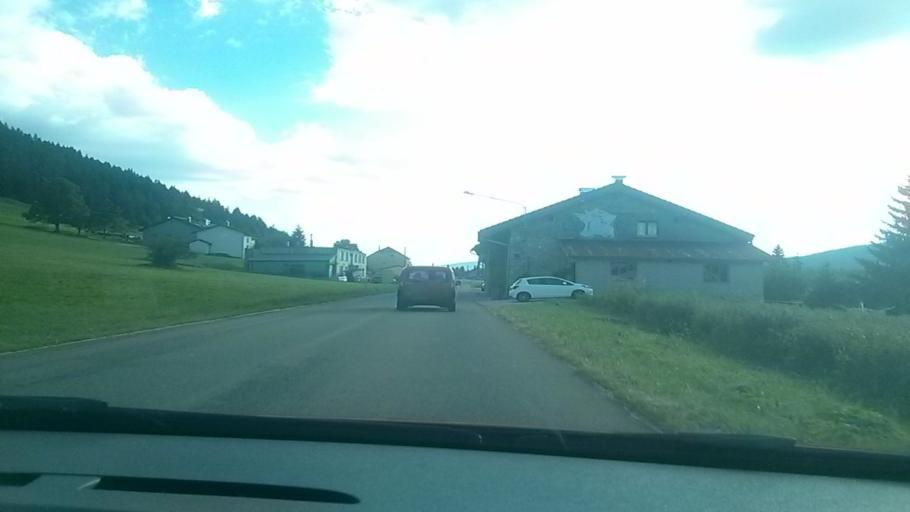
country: FR
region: Franche-Comte
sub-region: Departement du Jura
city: Les Rousses
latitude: 46.5211
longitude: 6.1234
